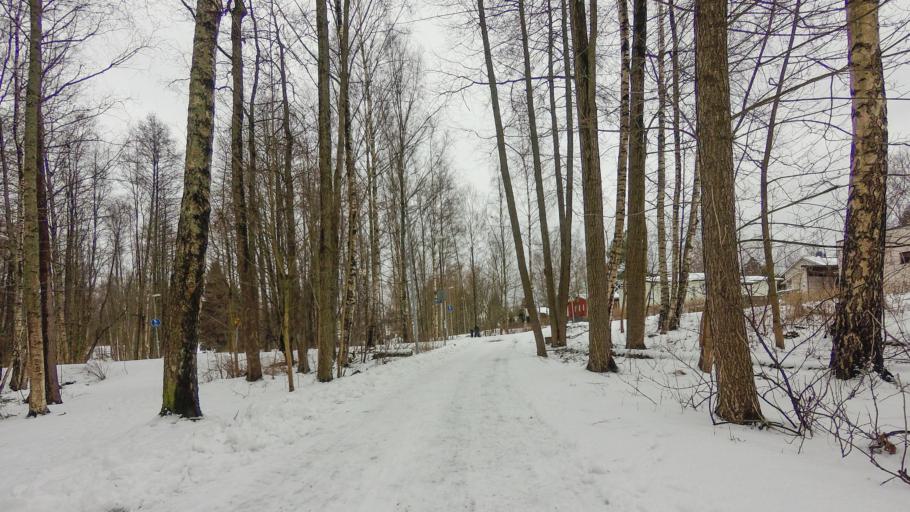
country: FI
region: Uusimaa
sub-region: Helsinki
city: Helsinki
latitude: 60.1719
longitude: 25.0564
